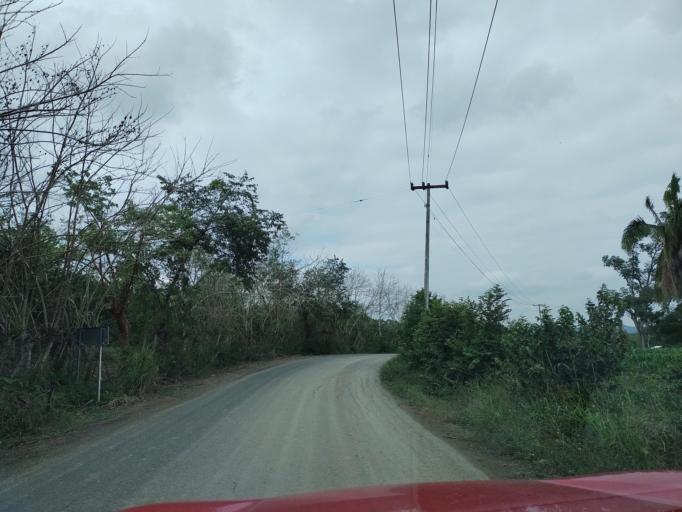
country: MX
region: Veracruz
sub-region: Coatzintla
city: Manuel Maria Contreras
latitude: 20.4463
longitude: -97.4436
